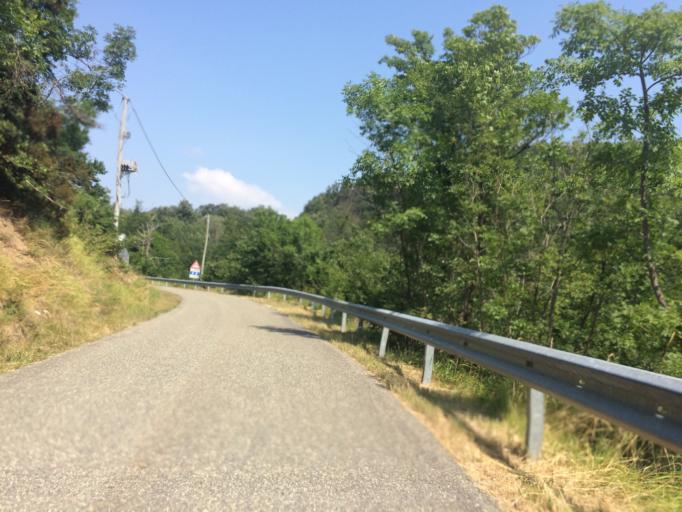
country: IT
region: Piedmont
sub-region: Provincia di Alessandria
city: Malvicino
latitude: 44.5378
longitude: 8.4114
